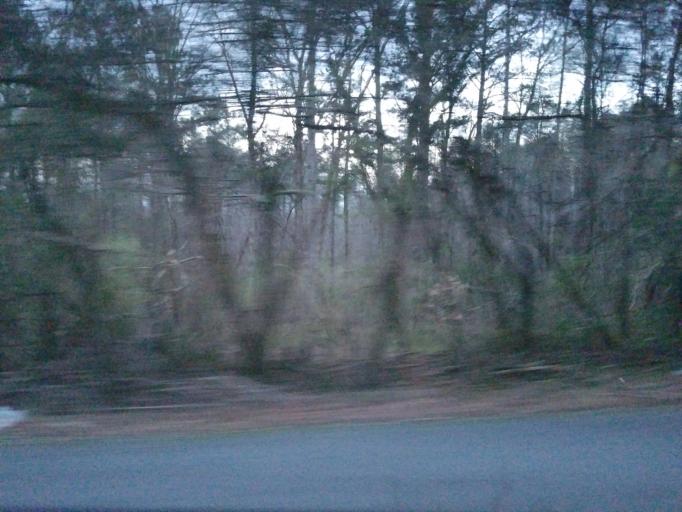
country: US
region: Georgia
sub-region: Cherokee County
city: Ball Ground
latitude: 34.3297
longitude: -84.3803
